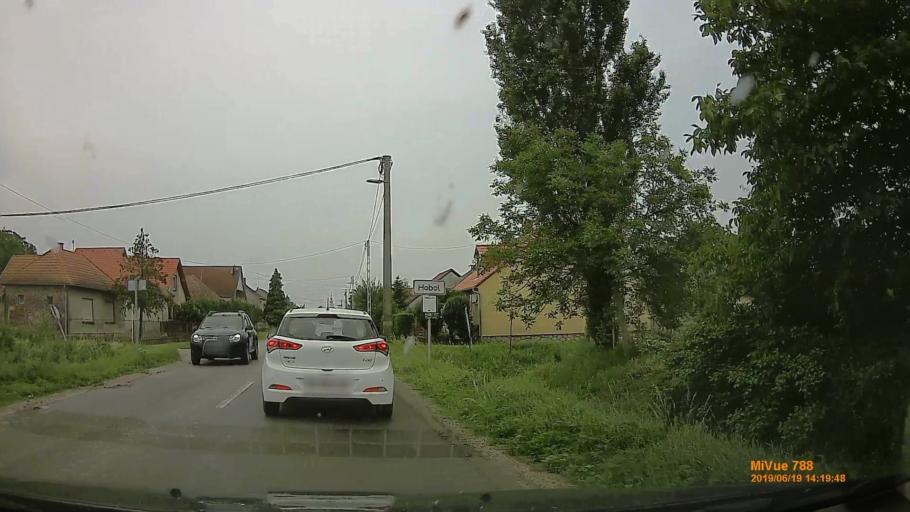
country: HU
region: Baranya
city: Szigetvar
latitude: 46.0292
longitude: 17.7791
